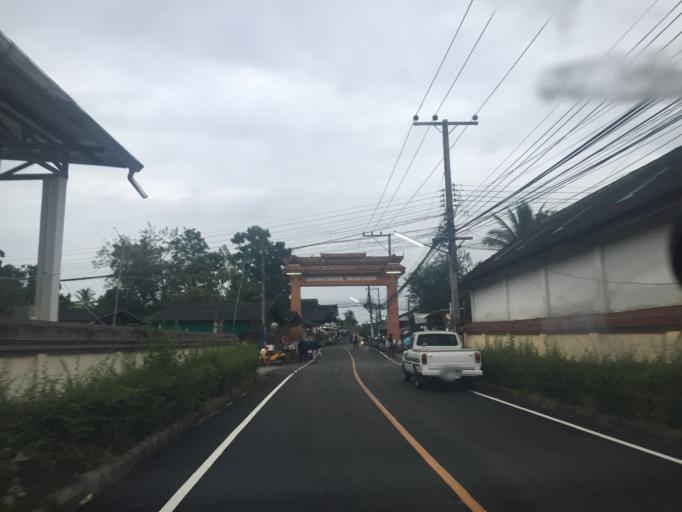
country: TH
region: Lamphun
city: Ban Thi
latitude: 18.6432
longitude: 99.0477
